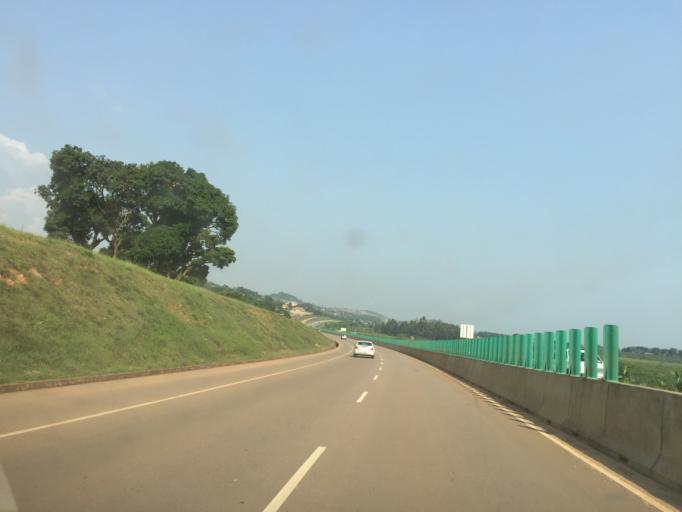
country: UG
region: Central Region
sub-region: Wakiso District
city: Kajansi
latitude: 0.2078
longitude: 32.5500
